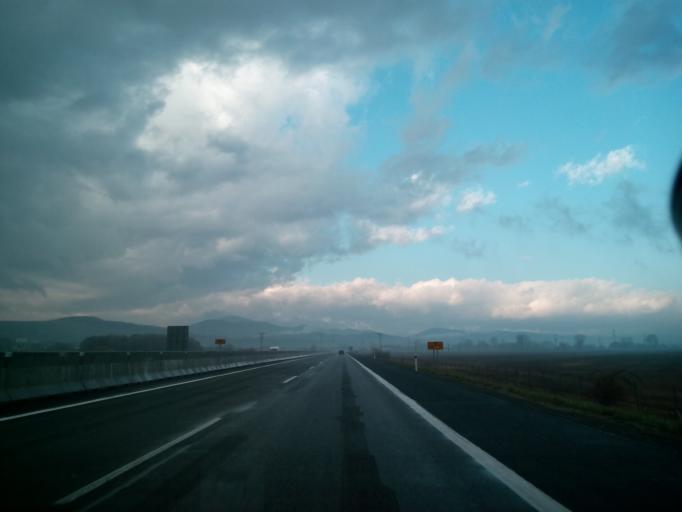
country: SK
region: Kosicky
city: Kosice
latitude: 48.8491
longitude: 21.2853
